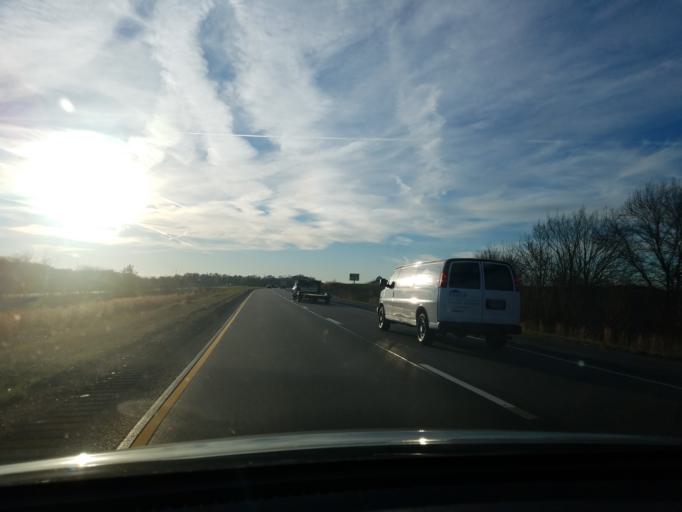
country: US
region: Indiana
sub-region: Dubois County
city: Ferdinand
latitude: 38.2039
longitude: -86.8214
